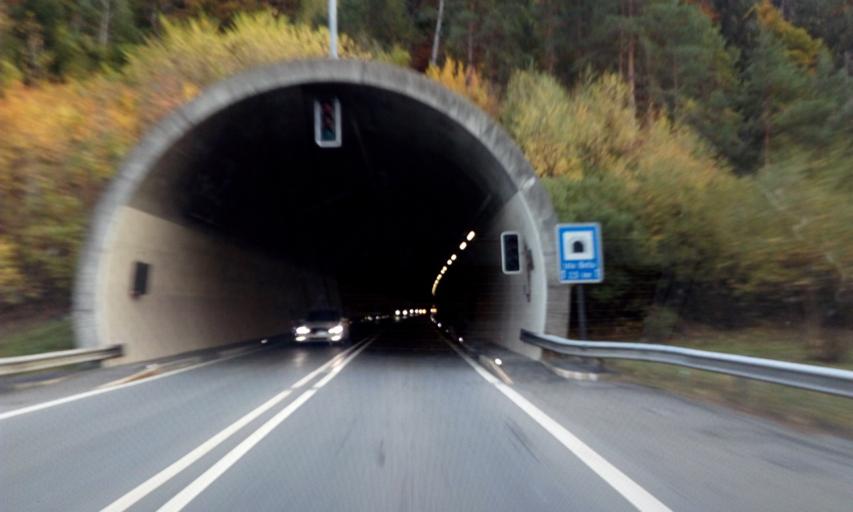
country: CH
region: Grisons
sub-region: Imboden District
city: Bonaduz
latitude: 46.8060
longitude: 9.4143
